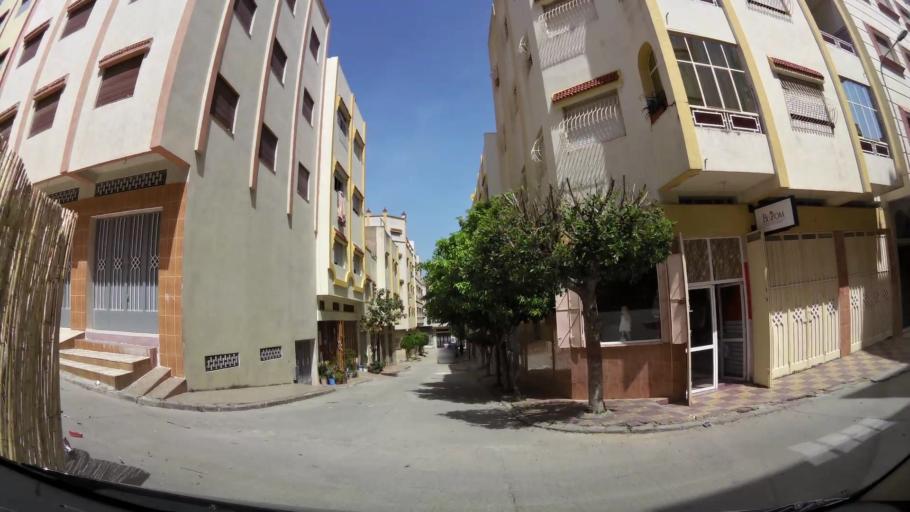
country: MA
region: Tanger-Tetouan
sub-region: Tanger-Assilah
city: Tangier
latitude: 35.7598
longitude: -5.8354
